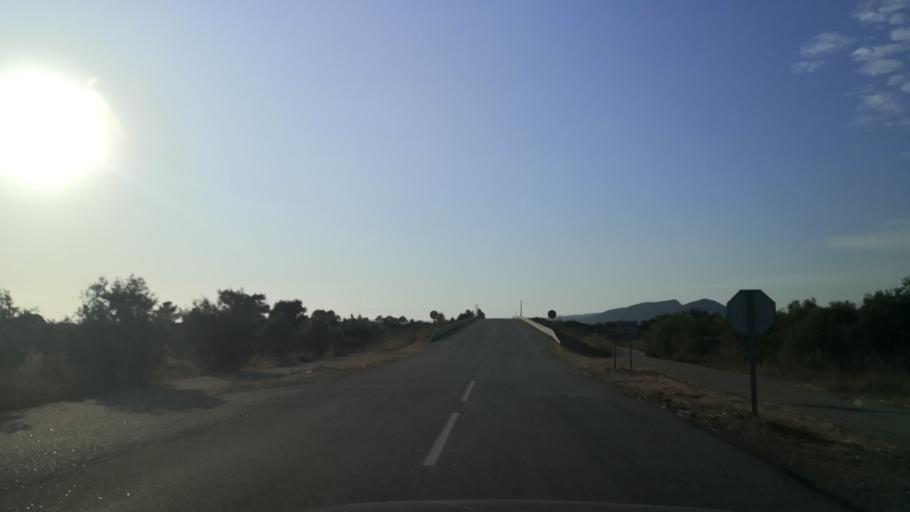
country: PT
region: Santarem
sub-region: Alcanena
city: Alcanena
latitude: 39.4541
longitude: -8.6279
